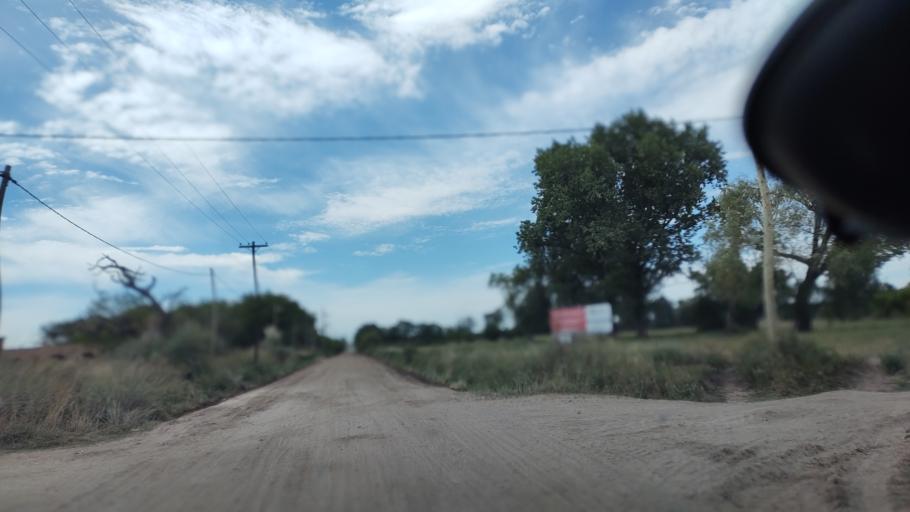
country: AR
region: Buenos Aires
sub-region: Partido de Lobos
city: Lobos
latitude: -35.1651
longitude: -59.1088
